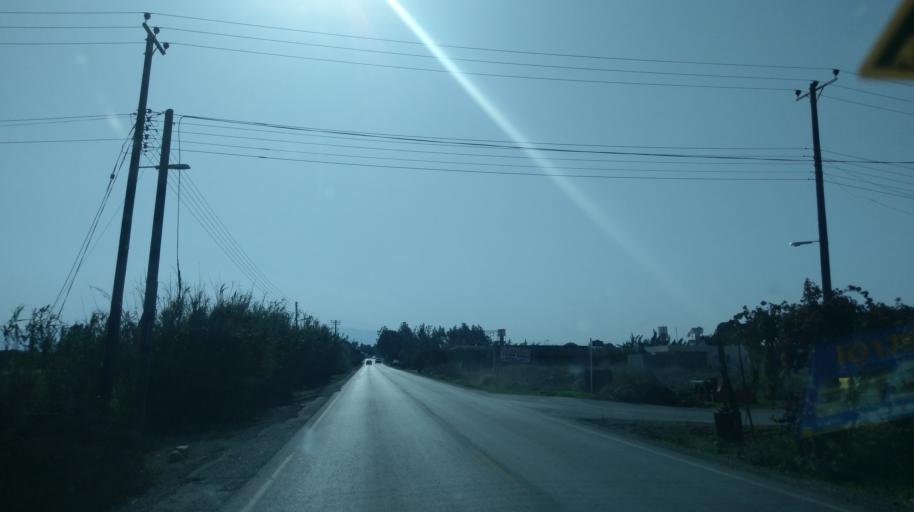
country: CY
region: Lefkosia
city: Morfou
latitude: 35.2112
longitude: 33.0020
